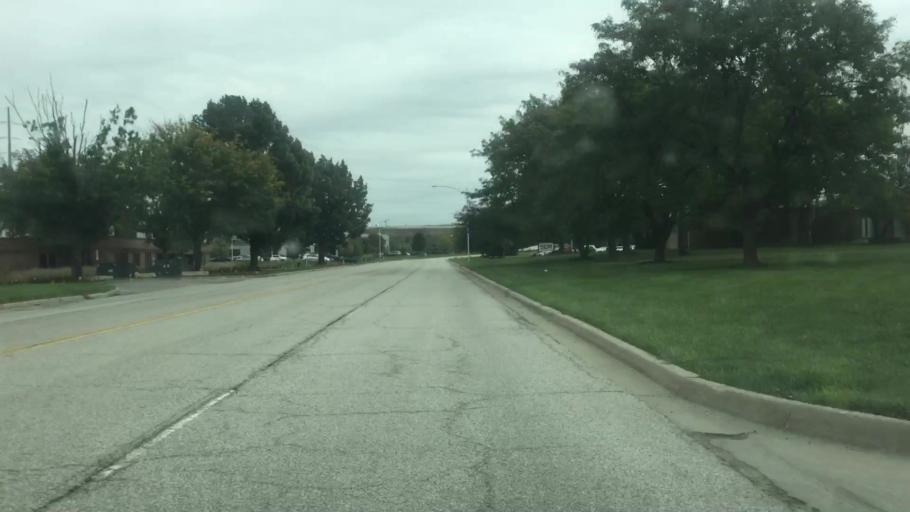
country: US
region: Kansas
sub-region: Johnson County
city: Lenexa
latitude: 38.9399
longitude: -94.7563
